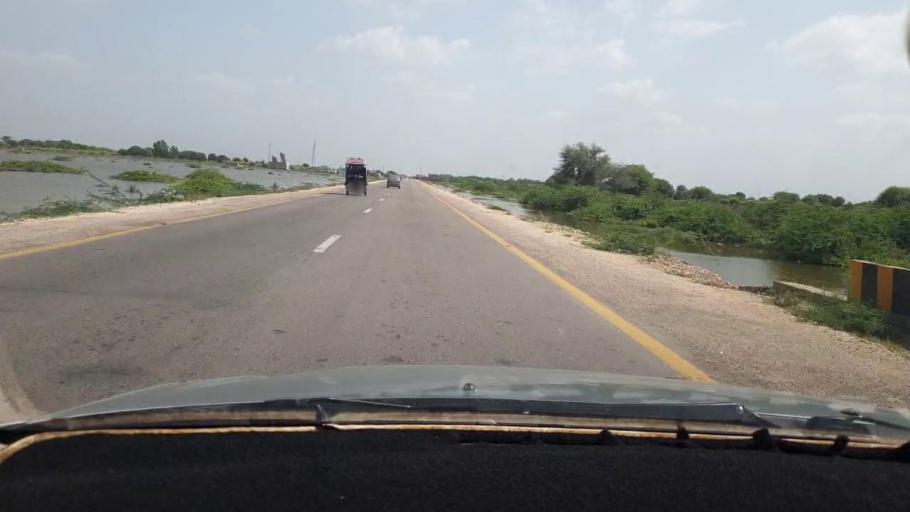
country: PK
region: Sindh
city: Digri
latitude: 25.1226
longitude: 69.1483
